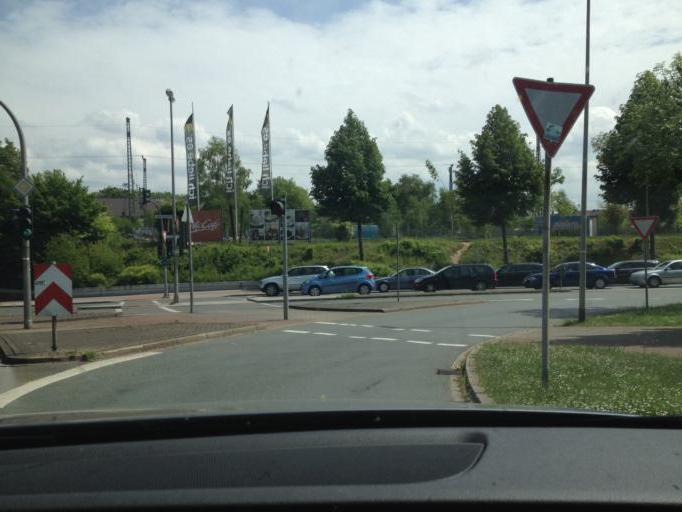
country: DE
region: North Rhine-Westphalia
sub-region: Regierungsbezirk Dusseldorf
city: Hochfeld
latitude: 51.3711
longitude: 6.7756
